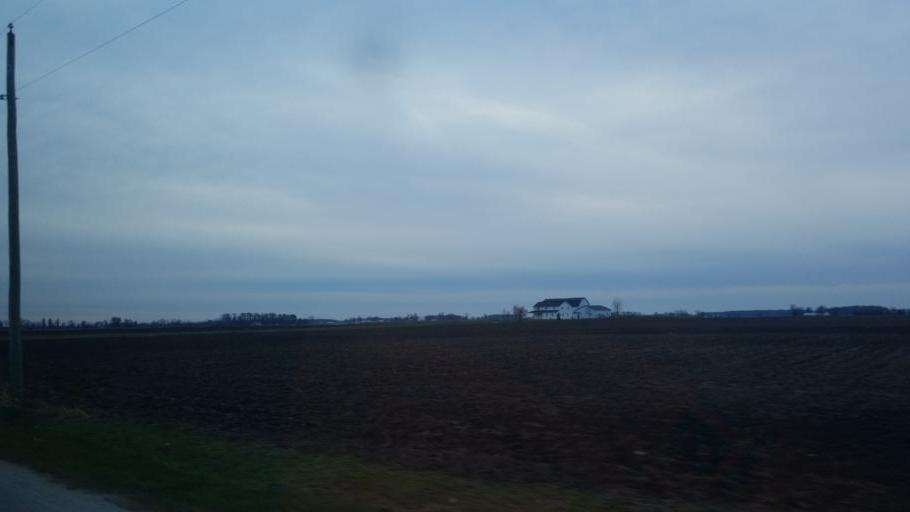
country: US
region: Indiana
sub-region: Adams County
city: Decatur
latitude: 40.7838
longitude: -84.8800
